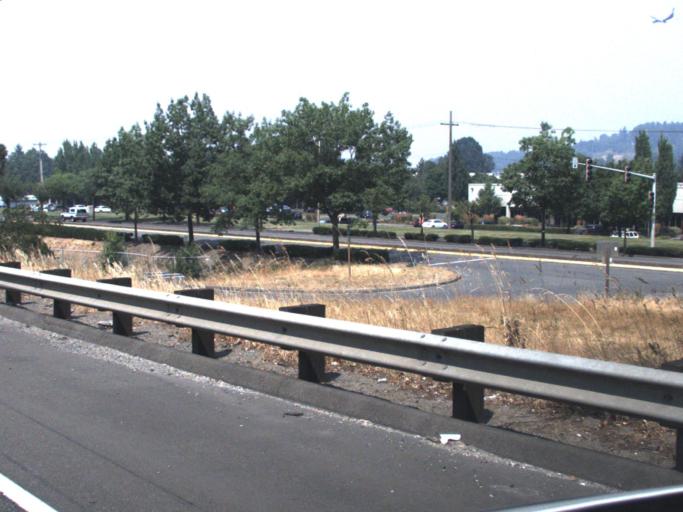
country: US
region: Washington
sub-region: King County
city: Riverton
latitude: 47.4863
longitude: -122.2762
